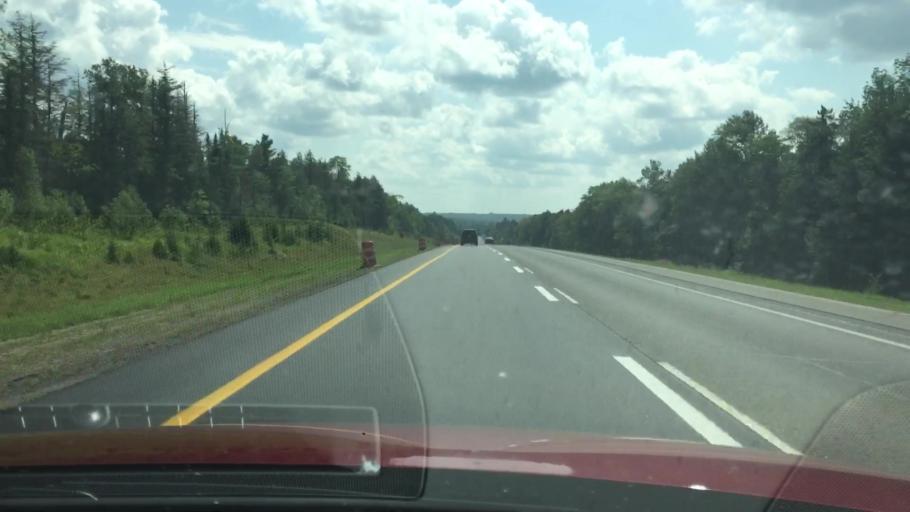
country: US
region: Maine
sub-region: Penobscot County
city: Medway
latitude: 45.6569
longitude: -68.4995
